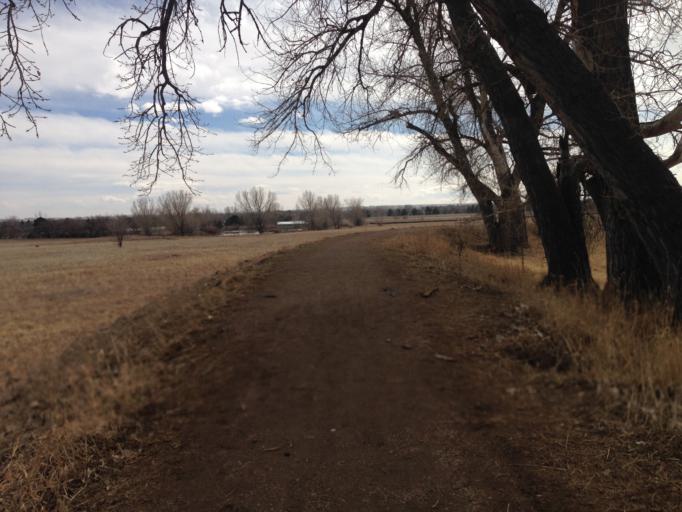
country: US
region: Colorado
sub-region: Boulder County
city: Louisville
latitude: 39.9716
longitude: -105.1441
